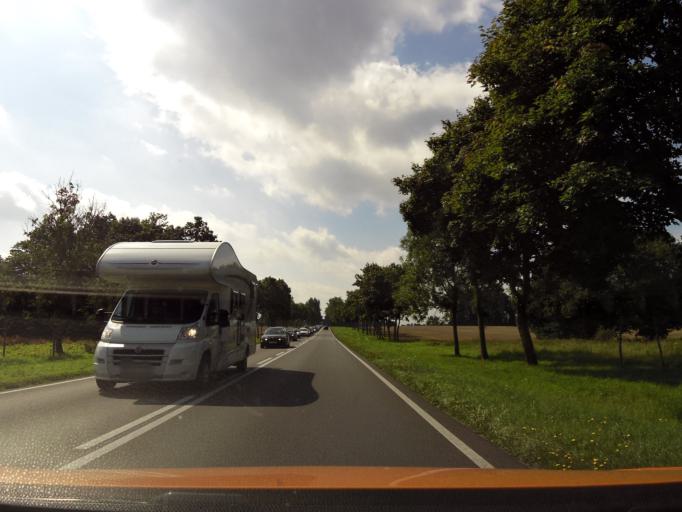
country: PL
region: West Pomeranian Voivodeship
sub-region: Powiat gryficki
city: Ploty
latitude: 53.7875
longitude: 15.2515
